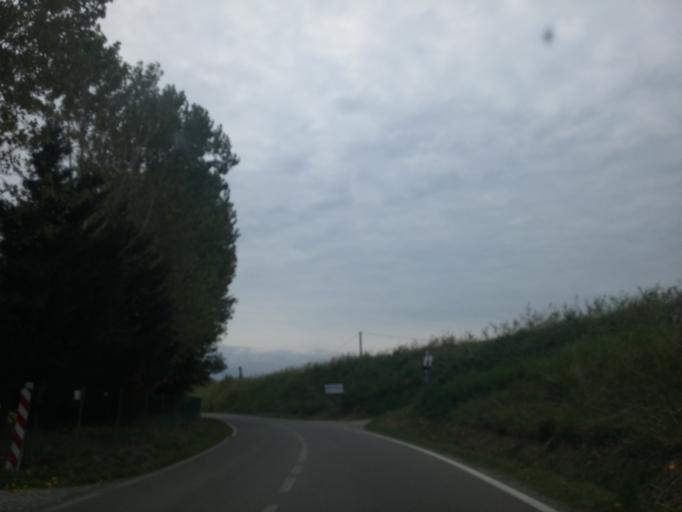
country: IT
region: Emilia-Romagna
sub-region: Provincia di Bologna
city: Longara
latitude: 44.5995
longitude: 11.3169
